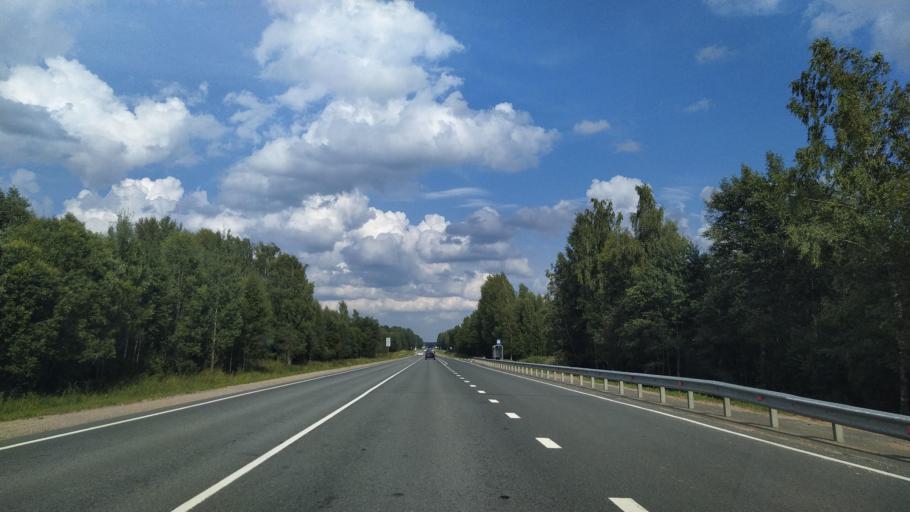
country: RU
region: Novgorod
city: Sol'tsy
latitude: 58.1688
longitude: 30.4833
